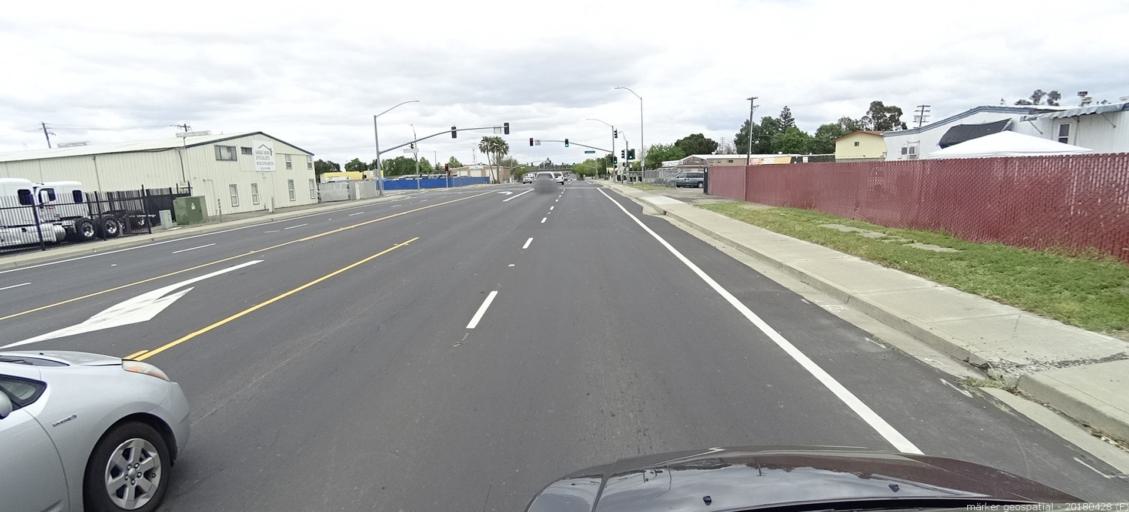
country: US
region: California
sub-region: Yolo County
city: West Sacramento
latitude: 38.5842
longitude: -121.5473
